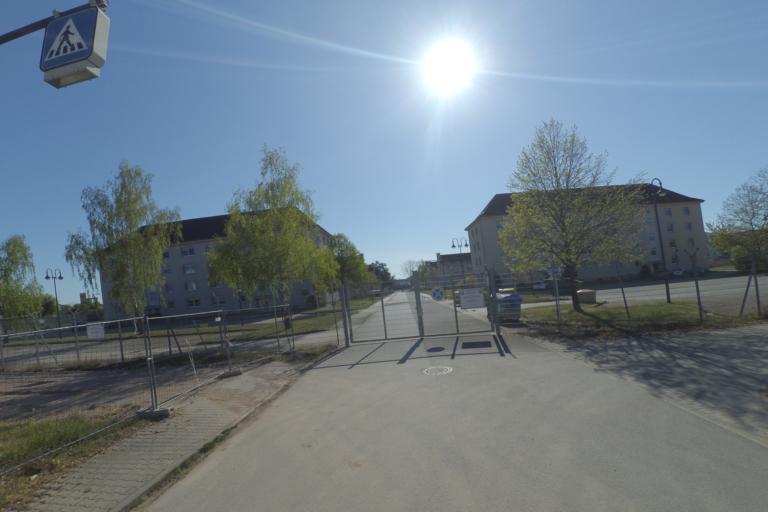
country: DE
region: Baden-Wuerttemberg
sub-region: Karlsruhe Region
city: Mannheim
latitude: 49.5139
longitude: 8.5304
